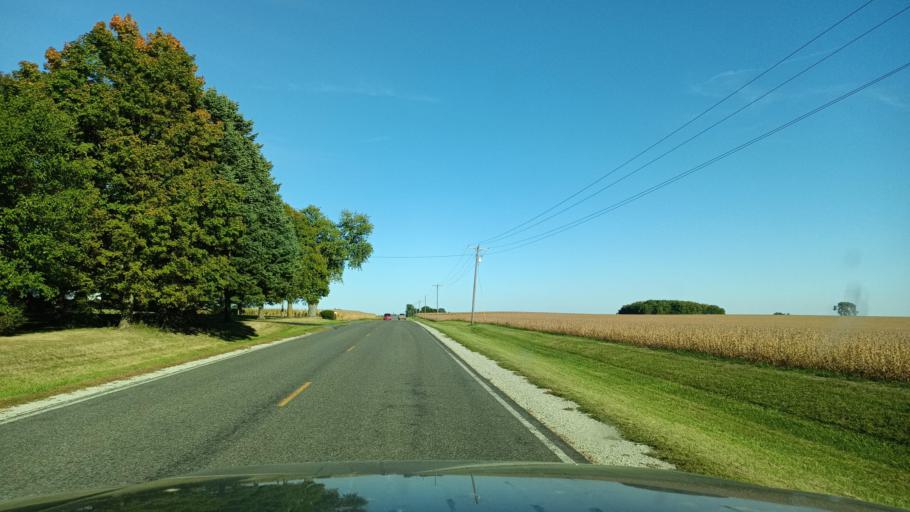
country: US
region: Illinois
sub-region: De Witt County
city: Clinton
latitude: 40.2244
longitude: -88.9157
